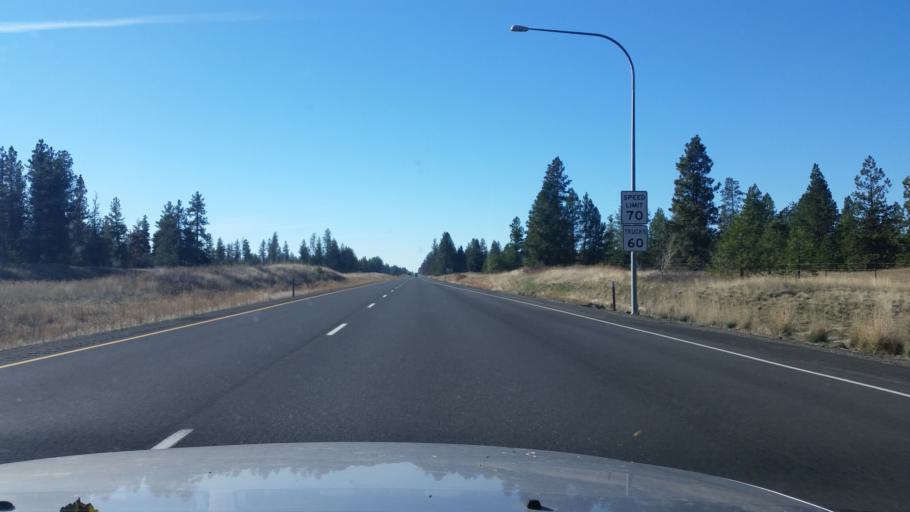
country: US
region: Washington
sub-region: Spokane County
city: Medical Lake
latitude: 47.5012
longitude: -117.6958
